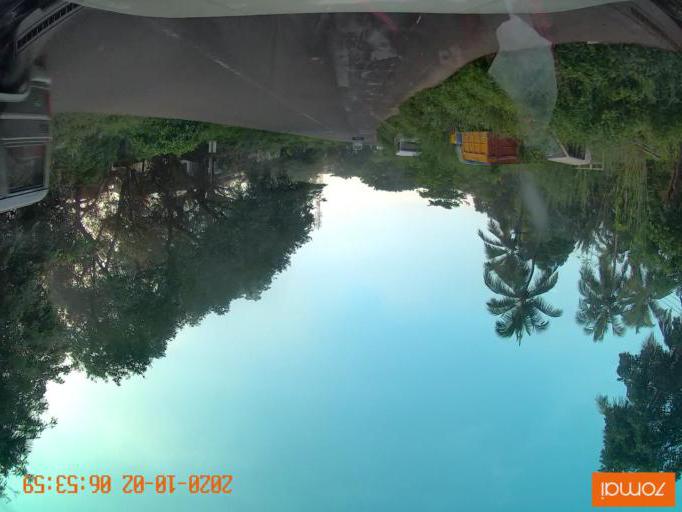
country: IN
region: Kerala
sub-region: Malappuram
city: Tirur
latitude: 10.8529
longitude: 76.0362
